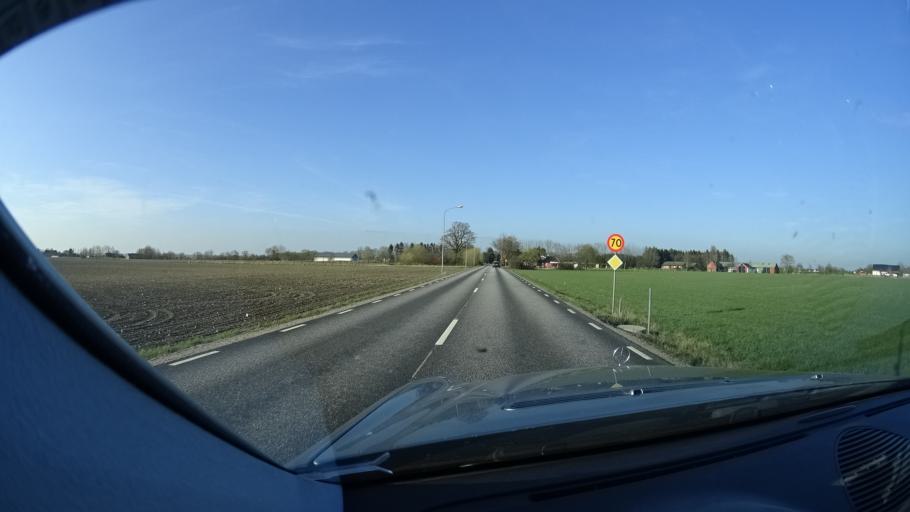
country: SE
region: Skane
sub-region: Eslovs Kommun
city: Eslov
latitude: 55.8480
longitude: 13.3435
